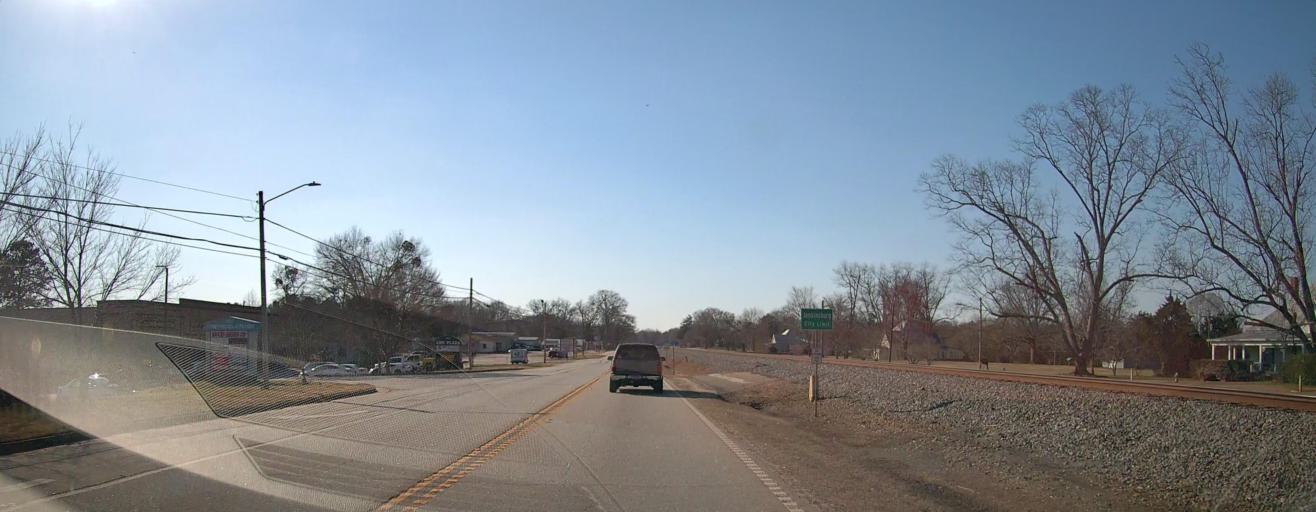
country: US
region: Georgia
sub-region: Butts County
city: Jackson
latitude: 33.3234
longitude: -84.0257
